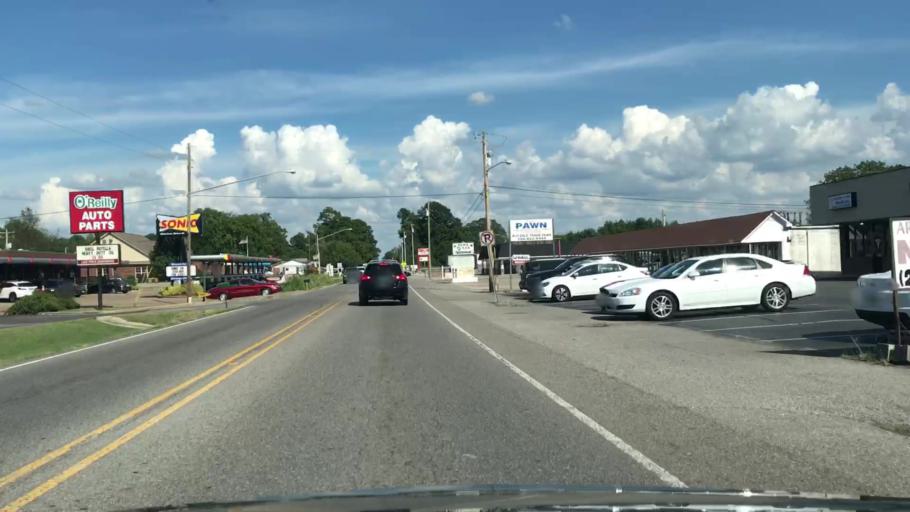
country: US
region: Tennessee
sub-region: Giles County
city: Ardmore
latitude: 34.9934
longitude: -86.8401
